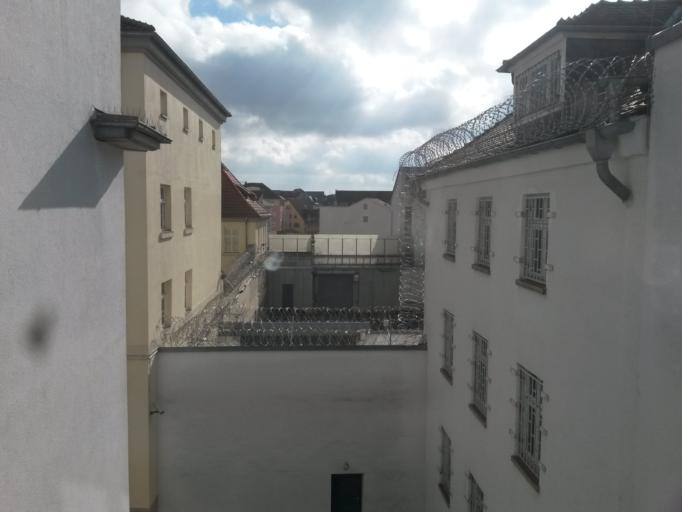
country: DE
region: Hesse
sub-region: Regierungsbezirk Kassel
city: Fulda
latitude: 50.5508
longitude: 9.6723
